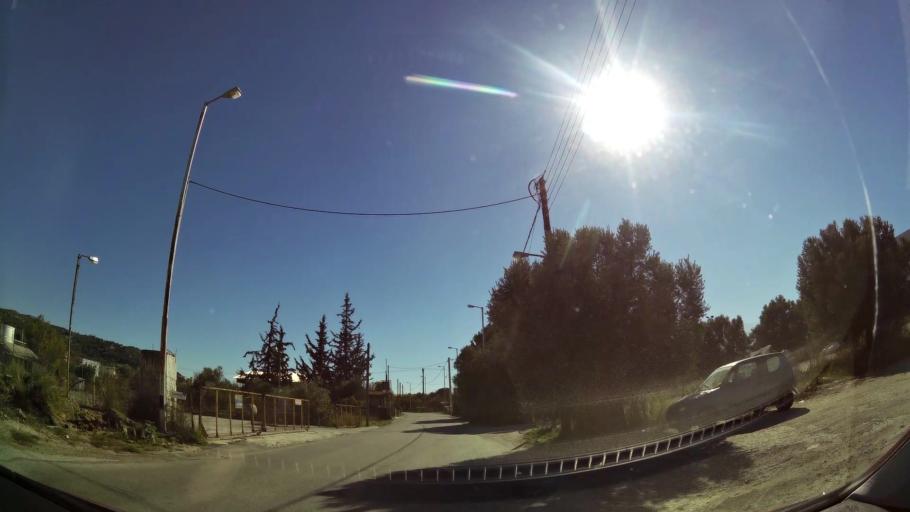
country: GR
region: Attica
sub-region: Nomarchia Anatolikis Attikis
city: Paiania
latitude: 37.9692
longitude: 23.8624
